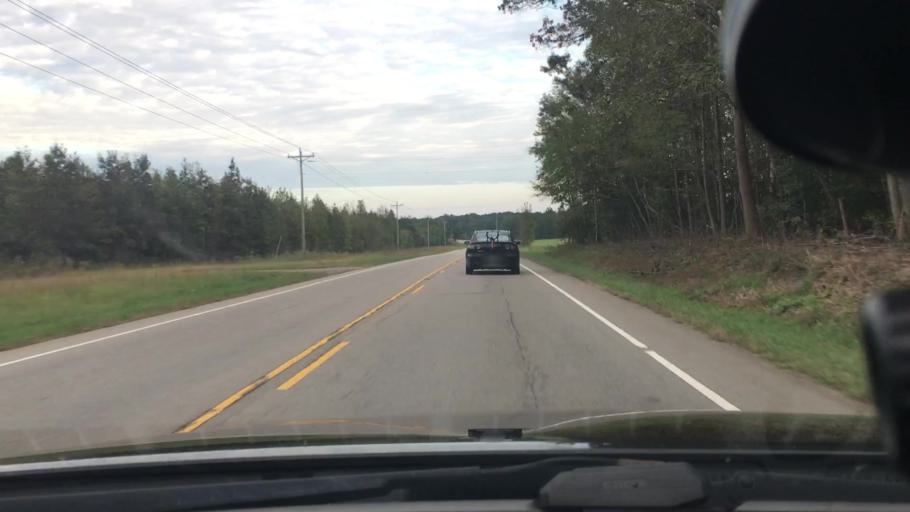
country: US
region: North Carolina
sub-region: Moore County
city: Robbins
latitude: 35.4004
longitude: -79.5525
